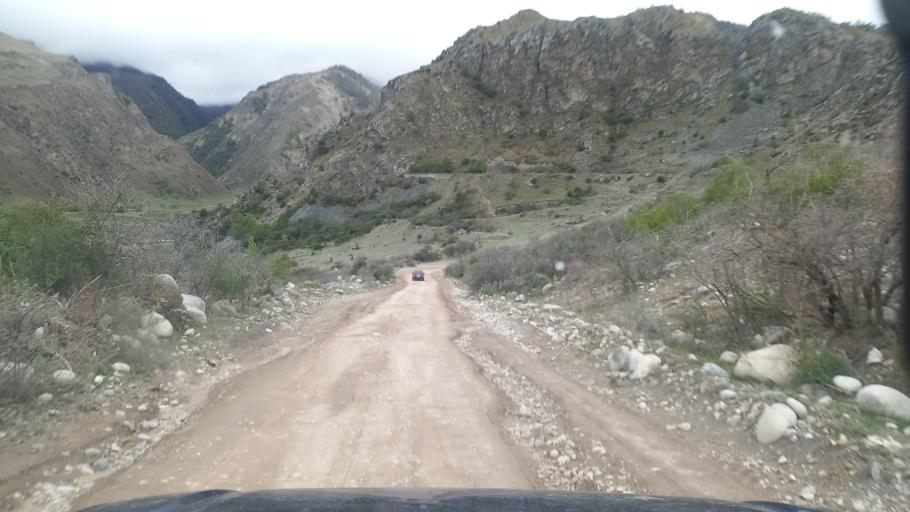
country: RU
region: Kabardino-Balkariya
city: Bylym
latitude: 43.4585
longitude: 43.0089
